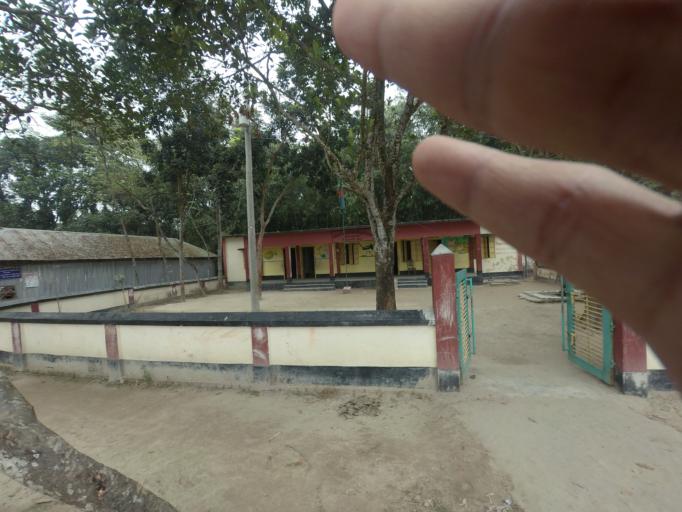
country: BD
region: Rajshahi
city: Saidpur
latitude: 26.0333
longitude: 88.8552
